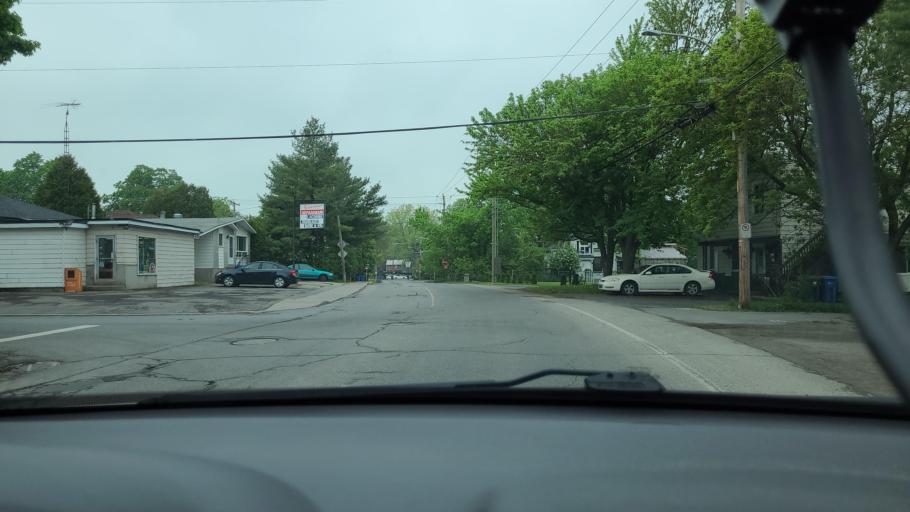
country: CA
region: Quebec
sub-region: Monteregie
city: L'Ile-Perrot
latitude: 45.3928
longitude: -73.9458
